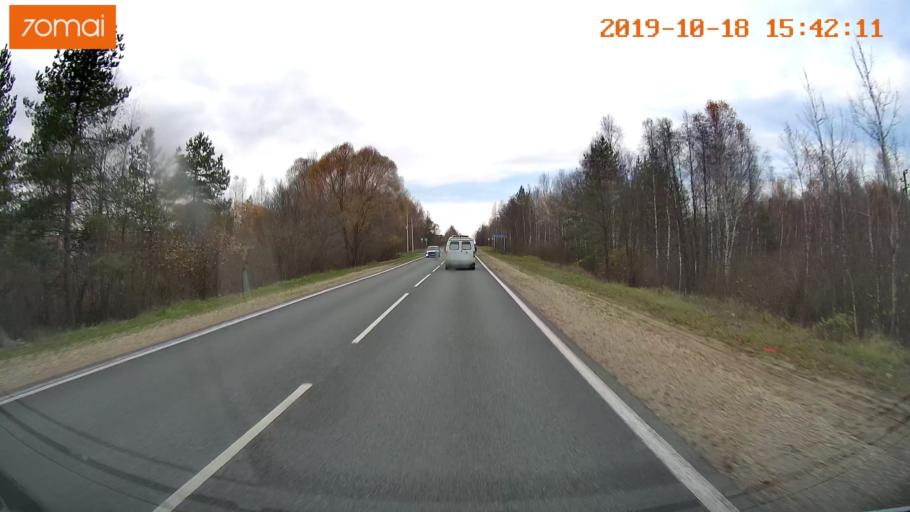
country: RU
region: Vladimir
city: Golovino
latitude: 55.9530
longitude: 40.5717
